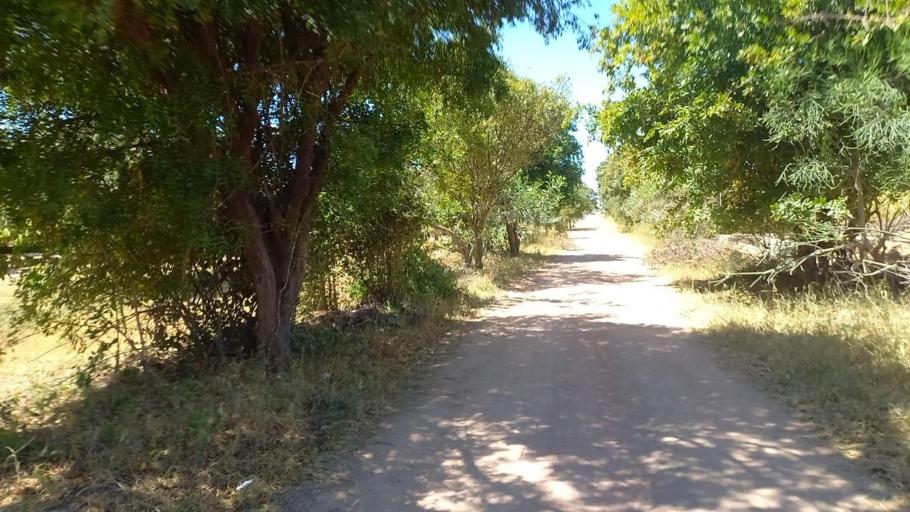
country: TZ
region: Dodoma
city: Dodoma
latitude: -6.1173
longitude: 35.7410
